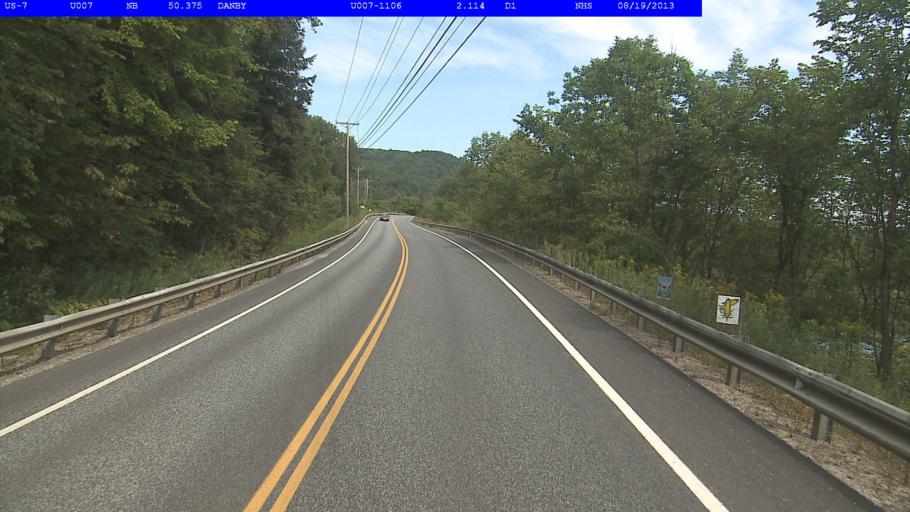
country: US
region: Vermont
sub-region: Rutland County
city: West Rutland
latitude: 43.3924
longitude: -72.9978
